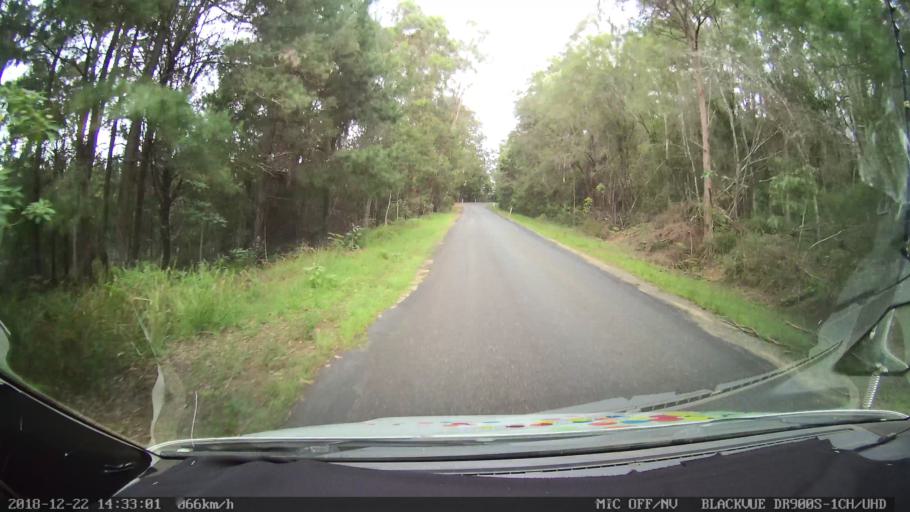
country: AU
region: New South Wales
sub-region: Bellingen
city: Dorrigo
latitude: -30.1095
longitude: 152.6240
